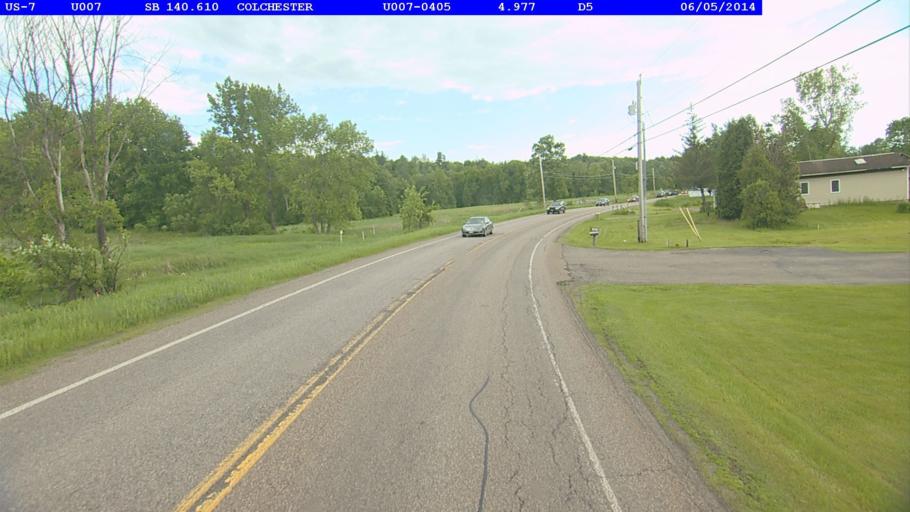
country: US
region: Vermont
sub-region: Chittenden County
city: Colchester
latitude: 44.5693
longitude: -73.1551
